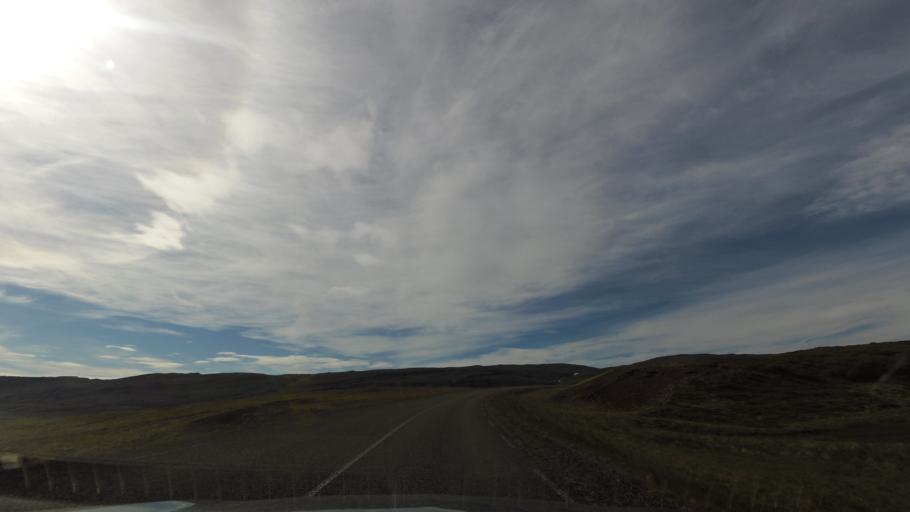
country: IS
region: West
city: Stykkisholmur
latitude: 65.5577
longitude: -22.1309
